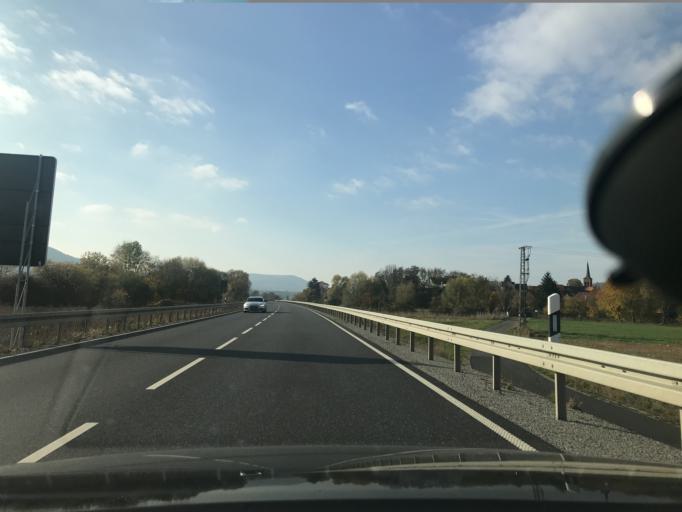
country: DE
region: Hesse
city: Wanfried
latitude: 51.1910
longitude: 10.1333
